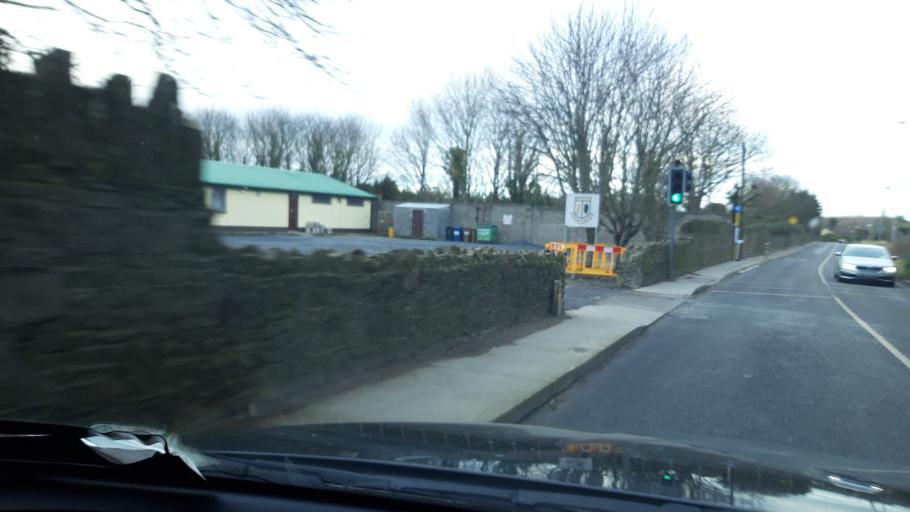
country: IE
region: Leinster
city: An Ros
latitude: 53.5293
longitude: -6.0914
